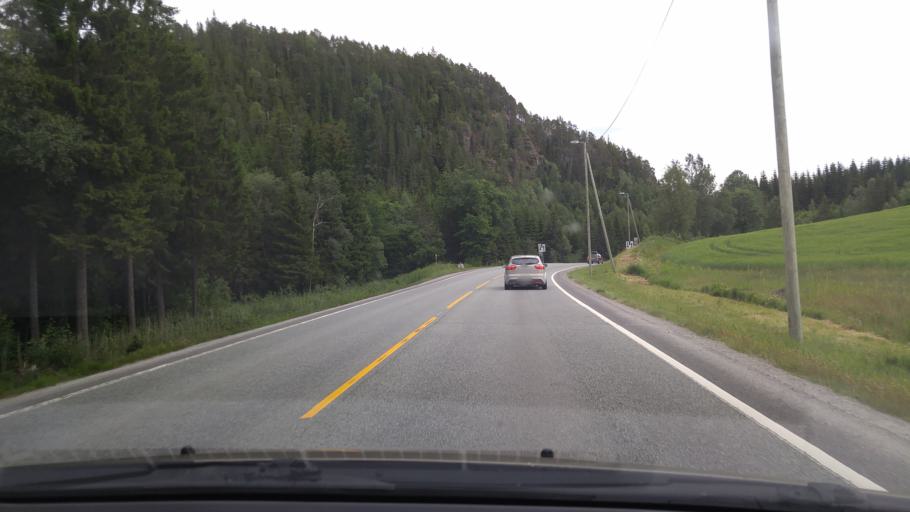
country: NO
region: Nord-Trondelag
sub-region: Steinkjer
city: Steinkjer
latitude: 64.0520
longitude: 11.4934
